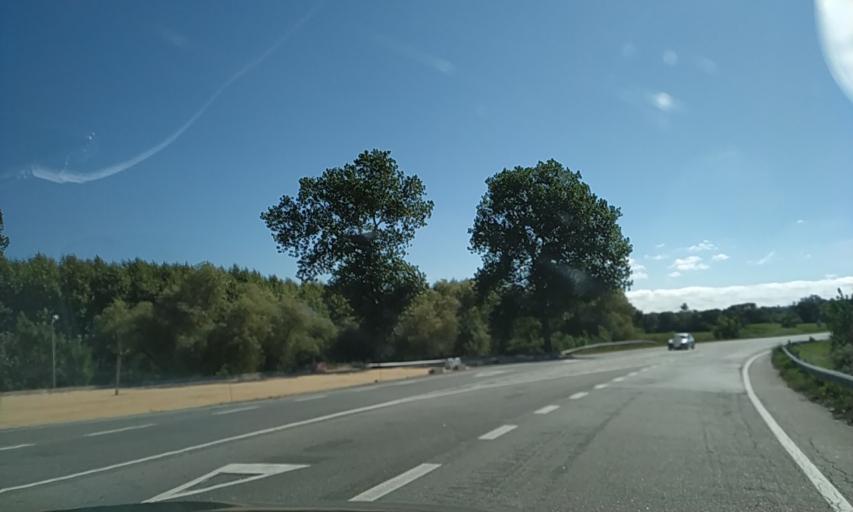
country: PT
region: Aveiro
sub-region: Estarreja
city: Salreu
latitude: 40.6856
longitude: -8.5591
